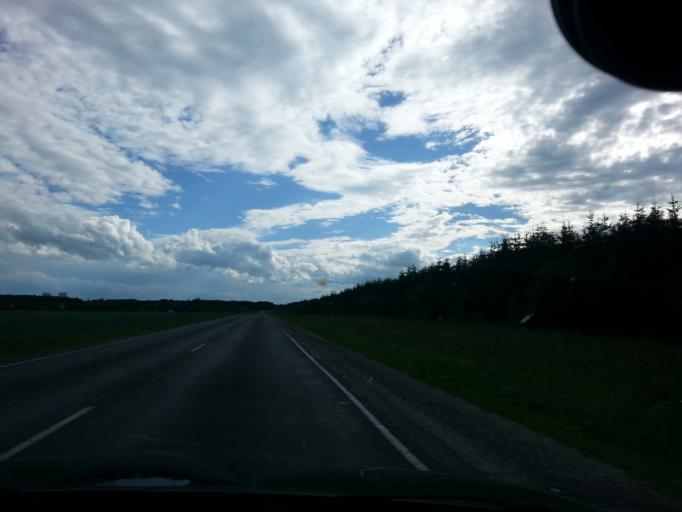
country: BY
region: Minsk
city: Svir
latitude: 54.8066
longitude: 26.1382
